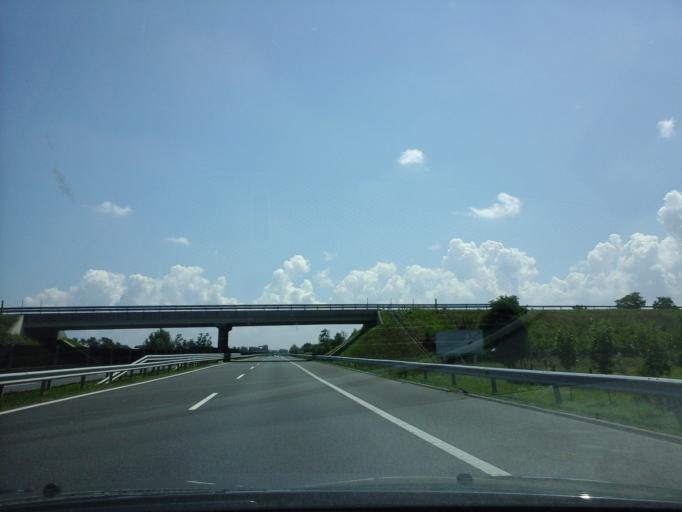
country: HU
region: Hajdu-Bihar
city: Hajduboszormeny
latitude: 47.6462
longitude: 21.4917
